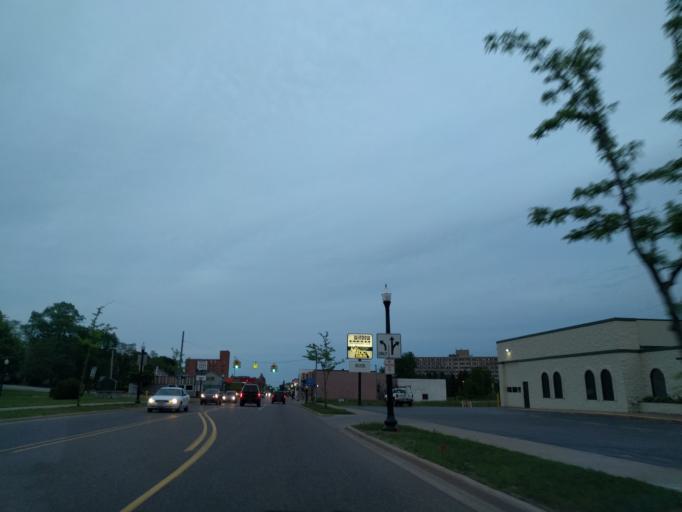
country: US
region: Michigan
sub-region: Marquette County
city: Marquette
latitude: 46.5450
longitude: -87.4051
